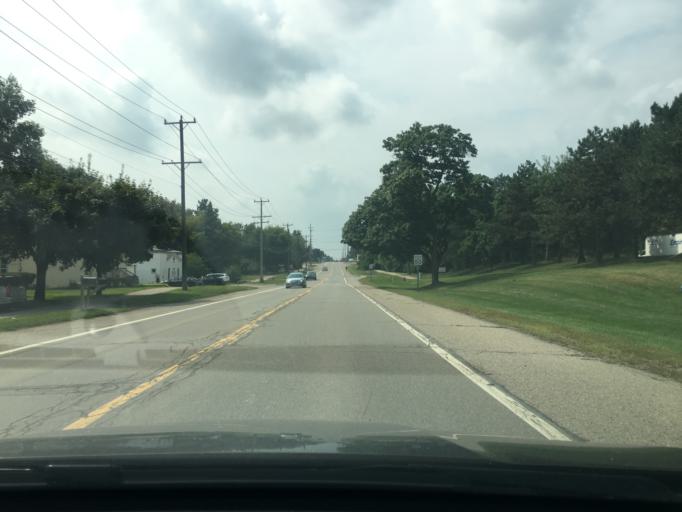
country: US
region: Michigan
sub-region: Oakland County
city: Rochester Hills
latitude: 42.6343
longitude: -83.2013
